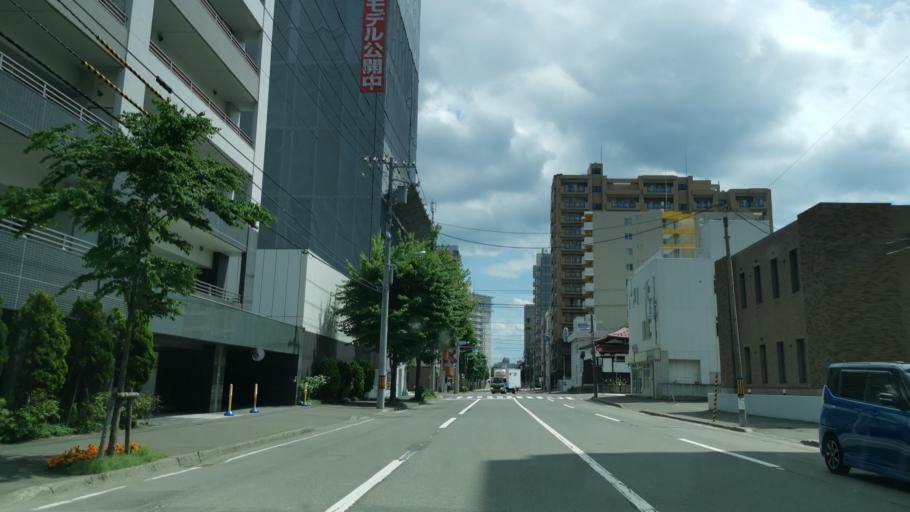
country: JP
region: Hokkaido
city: Sapporo
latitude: 43.0599
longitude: 141.3625
